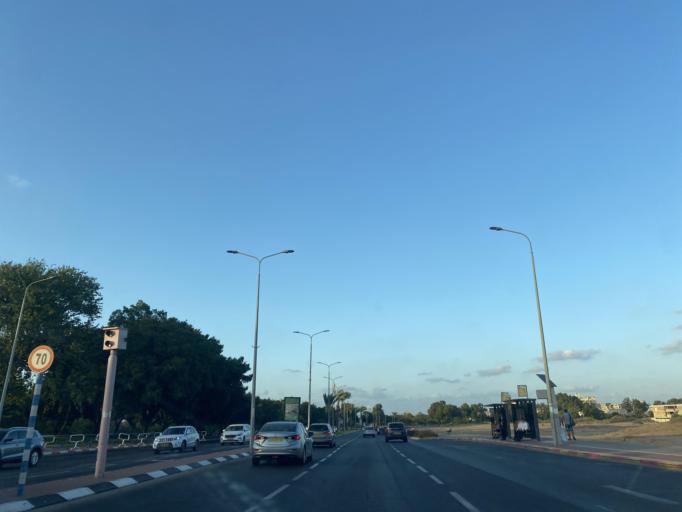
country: IL
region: Southern District
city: Ashdod
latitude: 31.7987
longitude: 34.6546
